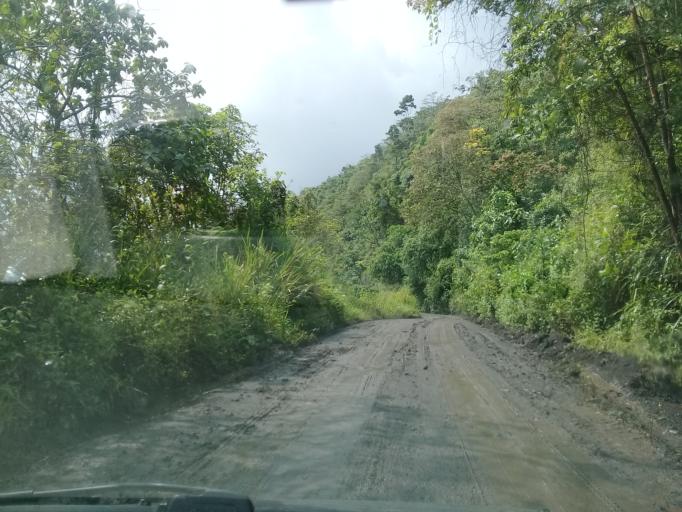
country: CO
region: Cundinamarca
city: Quipile
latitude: 4.7024
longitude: -74.5306
